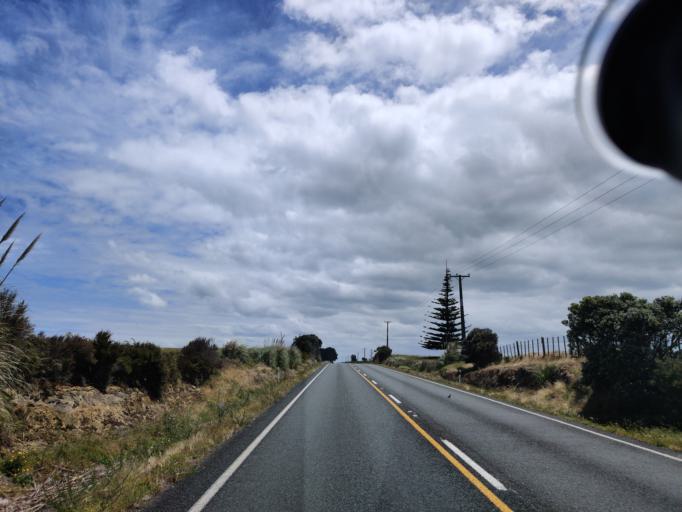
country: NZ
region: Northland
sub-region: Far North District
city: Kaitaia
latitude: -34.7000
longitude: 173.0274
